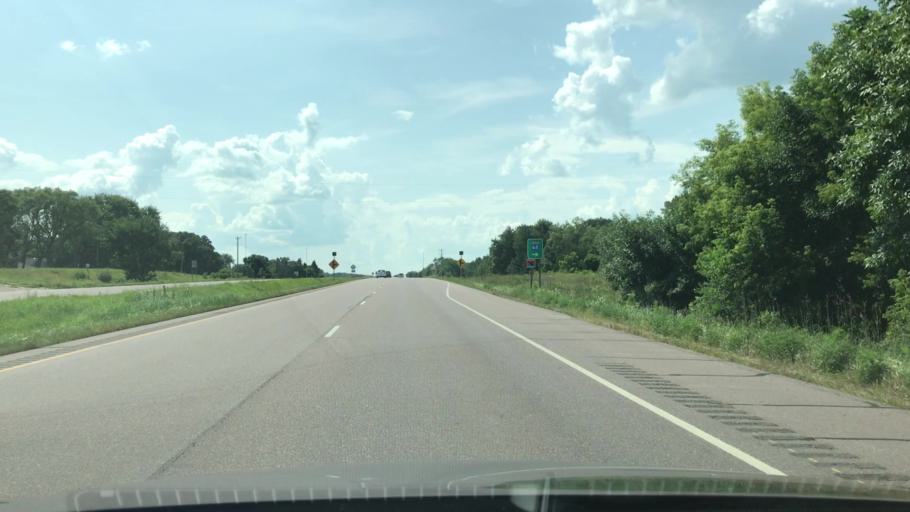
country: US
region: Minnesota
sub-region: Nicollet County
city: North Mankato
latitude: 44.1525
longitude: -94.0584
